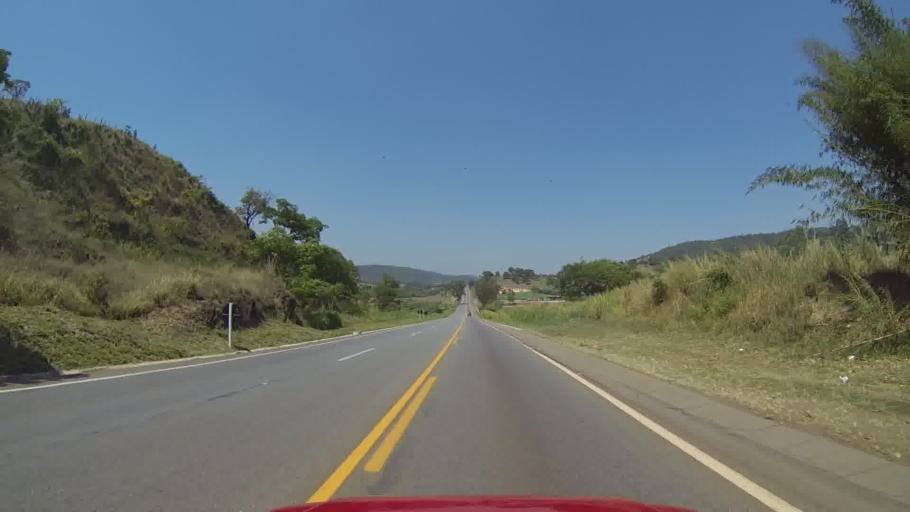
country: BR
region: Minas Gerais
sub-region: Itauna
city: Itauna
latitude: -20.0440
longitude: -44.5378
